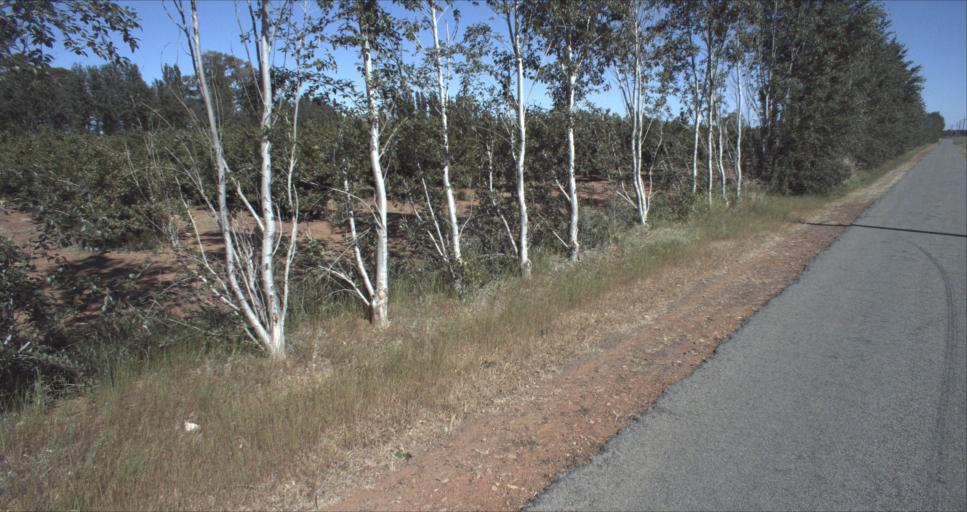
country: AU
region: New South Wales
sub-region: Leeton
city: Leeton
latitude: -34.5429
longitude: 146.3434
